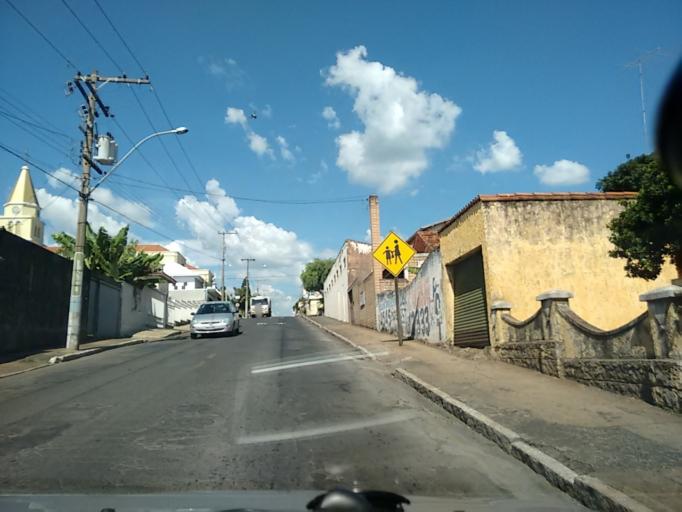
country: BR
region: Sao Paulo
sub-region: Pompeia
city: Pompeia
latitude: -22.1090
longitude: -50.1732
